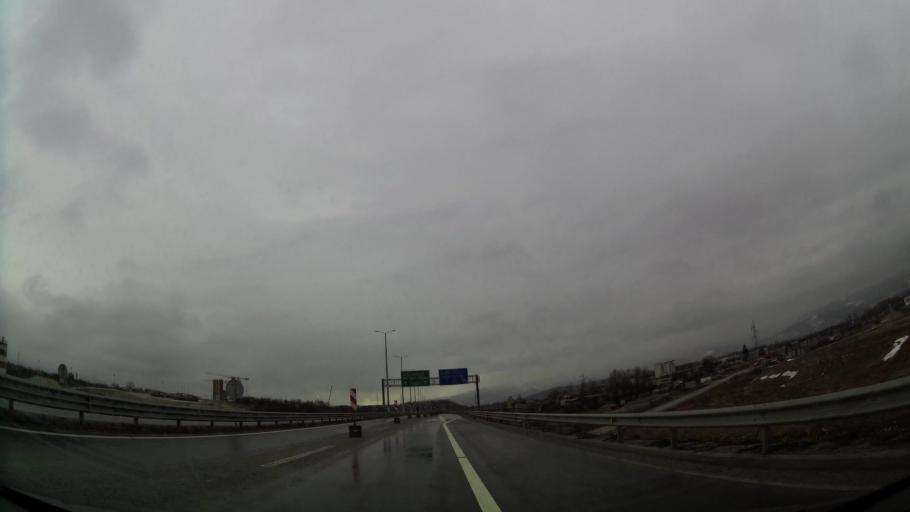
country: XK
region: Ferizaj
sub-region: Komuna e Kacanikut
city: Kacanik
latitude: 42.2806
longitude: 21.2102
